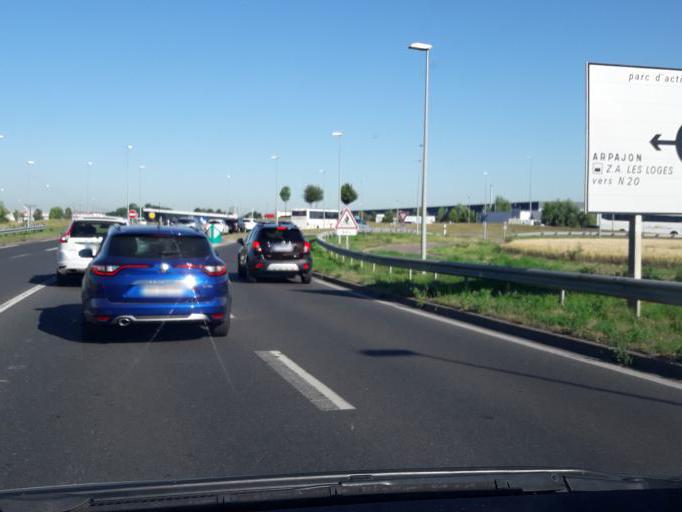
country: FR
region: Ile-de-France
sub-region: Departement de l'Essonne
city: Marolles-en-Hurepoix
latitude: 48.5776
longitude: 2.3005
